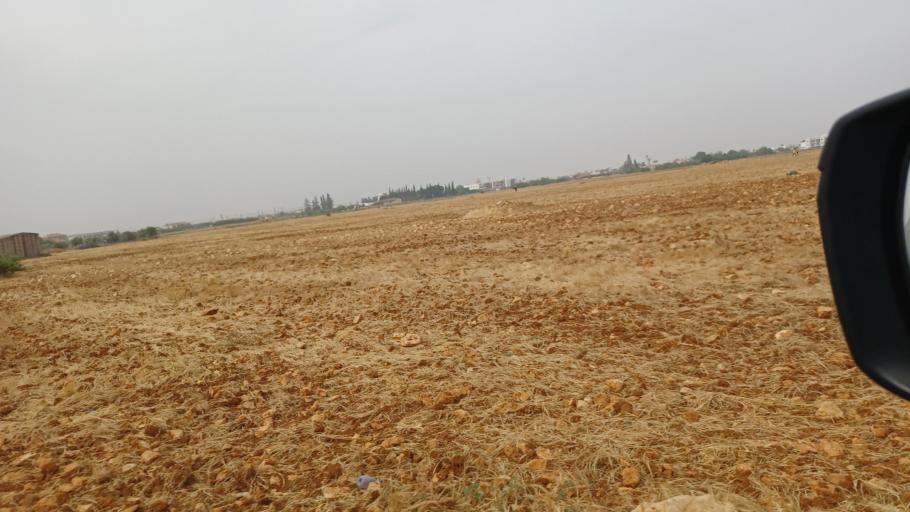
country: CY
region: Lefkosia
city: Kokkinotrimithia
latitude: 35.1539
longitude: 33.2198
